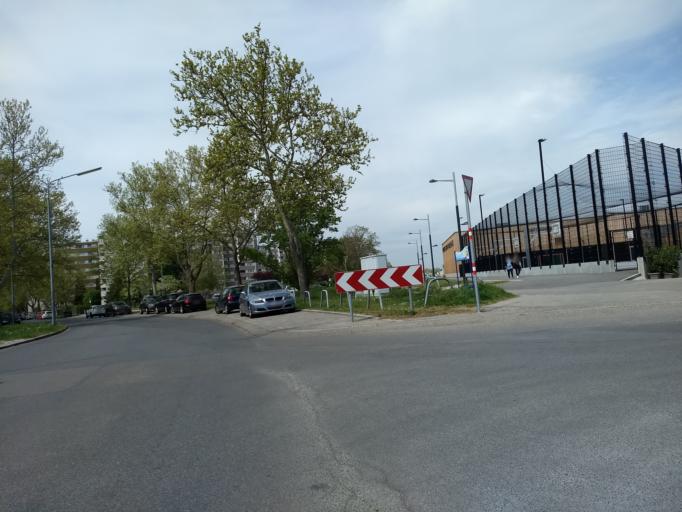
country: AT
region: Lower Austria
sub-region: Politischer Bezirk Wien-Umgebung
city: Gerasdorf bei Wien
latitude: 48.2400
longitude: 16.4901
